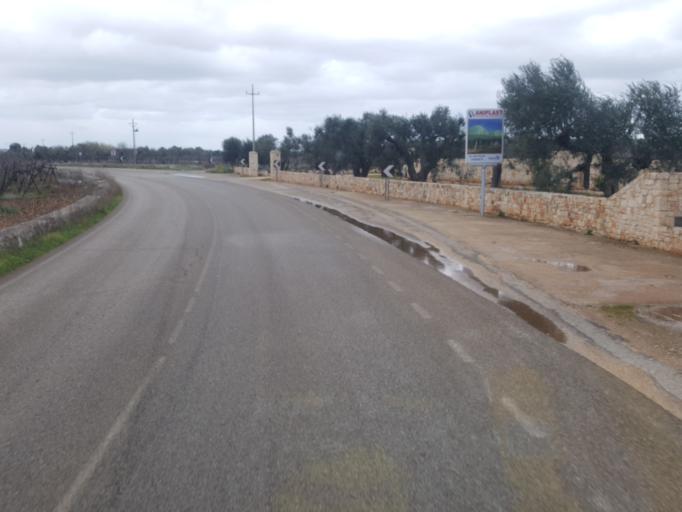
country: IT
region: Apulia
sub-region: Provincia di Bari
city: Conversano
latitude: 40.9523
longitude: 17.0915
